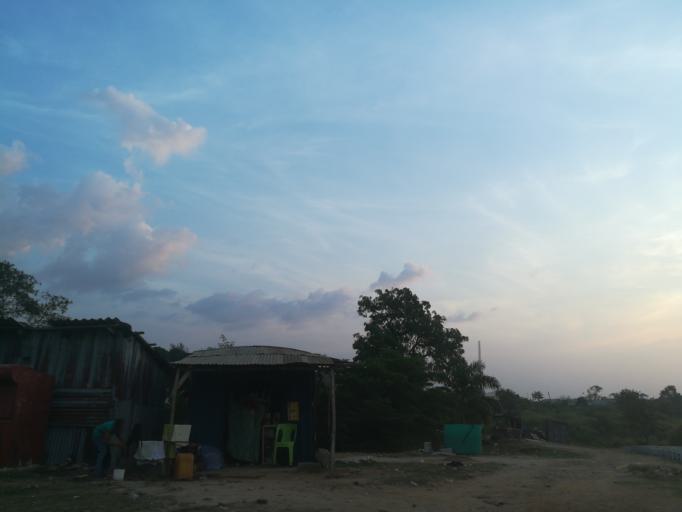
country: NG
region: Abuja Federal Capital Territory
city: Abuja
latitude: 9.0790
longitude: 7.3874
